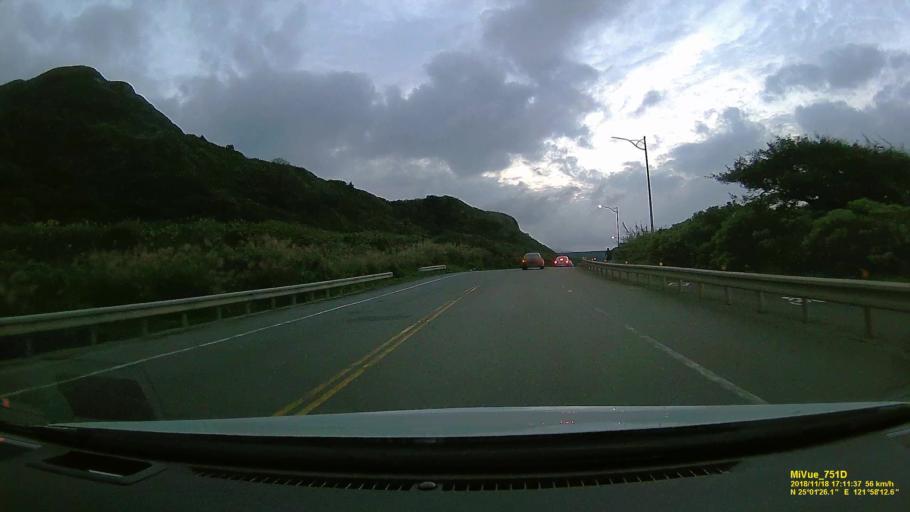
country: TW
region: Taiwan
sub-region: Keelung
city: Keelung
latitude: 25.0238
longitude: 121.9701
